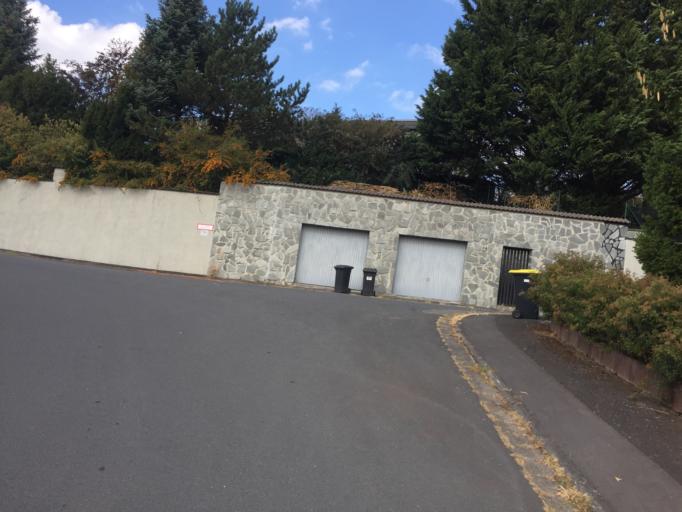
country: DE
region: Hesse
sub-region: Regierungsbezirk Giessen
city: Lich
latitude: 50.4821
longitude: 8.8310
